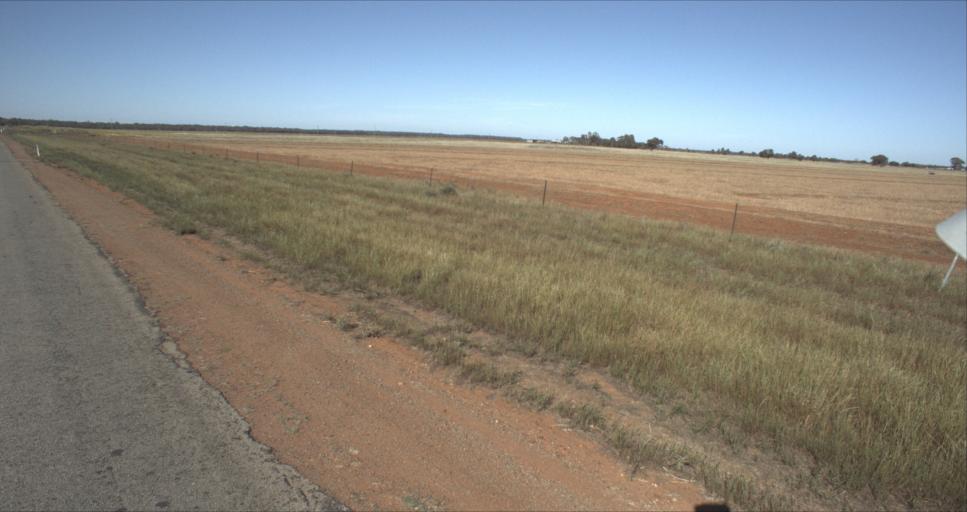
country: AU
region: New South Wales
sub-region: Leeton
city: Leeton
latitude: -34.5796
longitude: 146.3090
